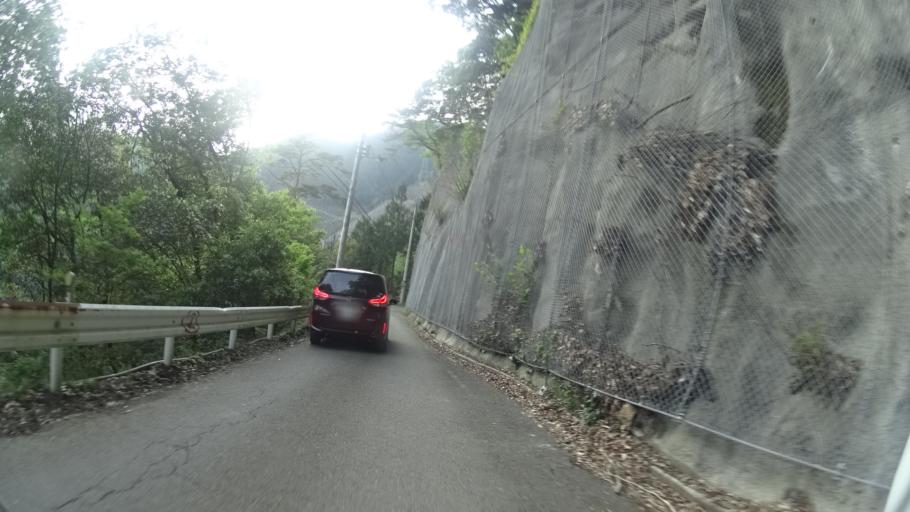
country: JP
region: Tokushima
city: Ikedacho
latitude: 33.9458
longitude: 133.8189
